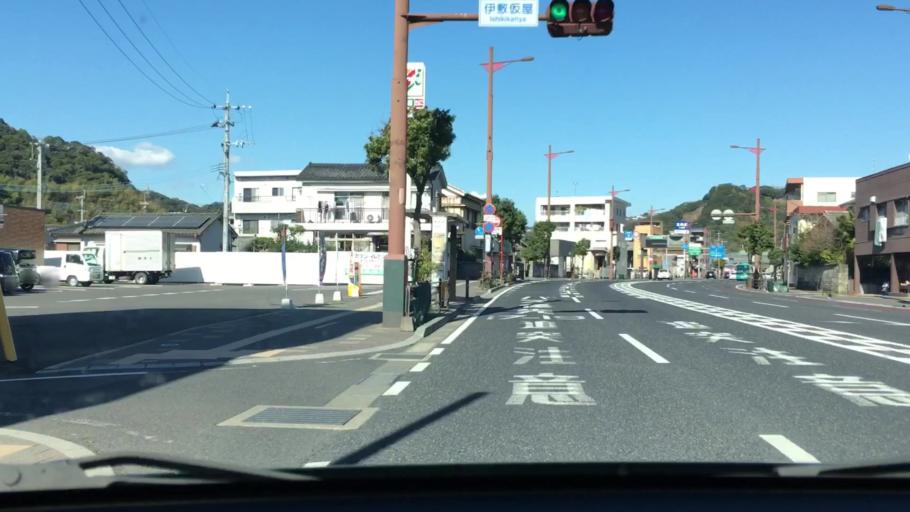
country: JP
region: Kagoshima
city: Kagoshima-shi
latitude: 31.6201
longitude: 130.5265
